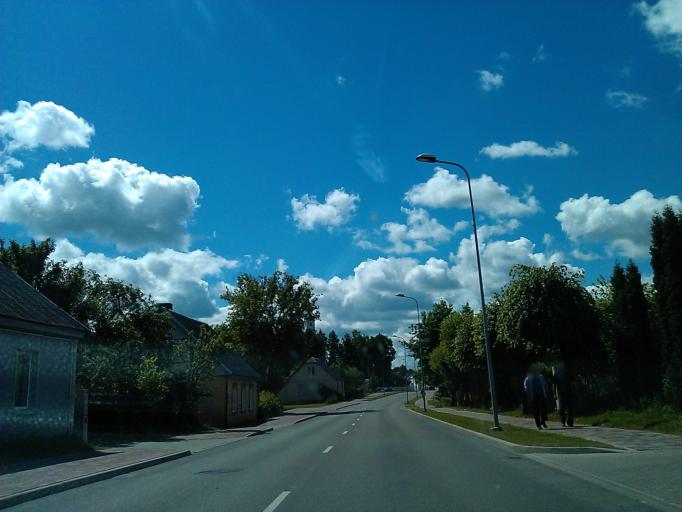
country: LV
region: Vilanu
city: Vilani
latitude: 56.5549
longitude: 26.9236
